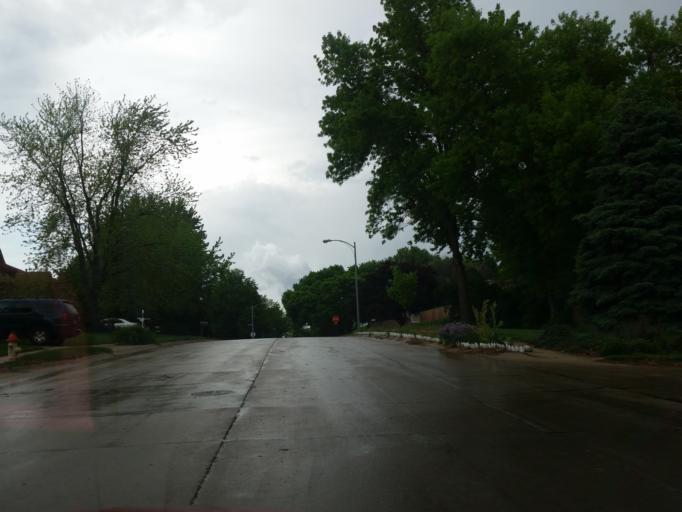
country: US
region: Nebraska
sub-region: Sarpy County
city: Offutt Air Force Base
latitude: 41.1157
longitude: -95.9709
